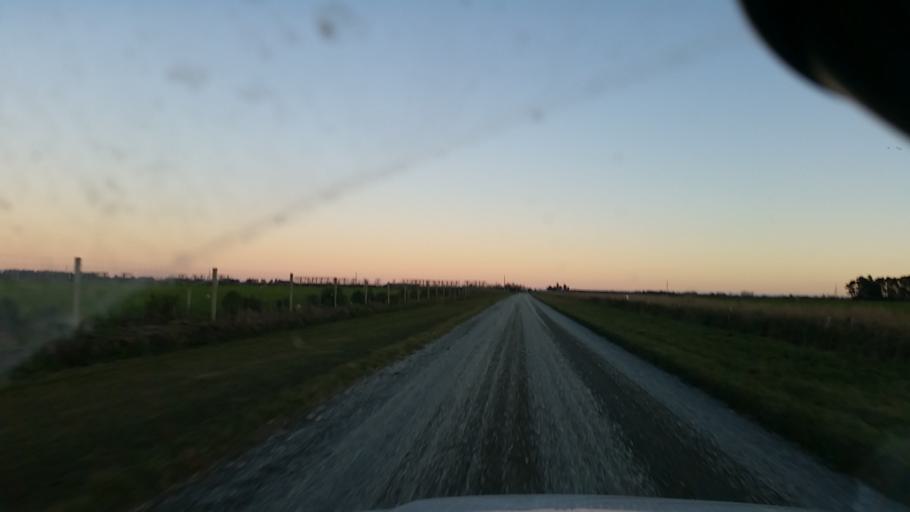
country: NZ
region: Canterbury
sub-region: Ashburton District
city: Tinwald
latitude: -44.0633
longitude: 171.6605
